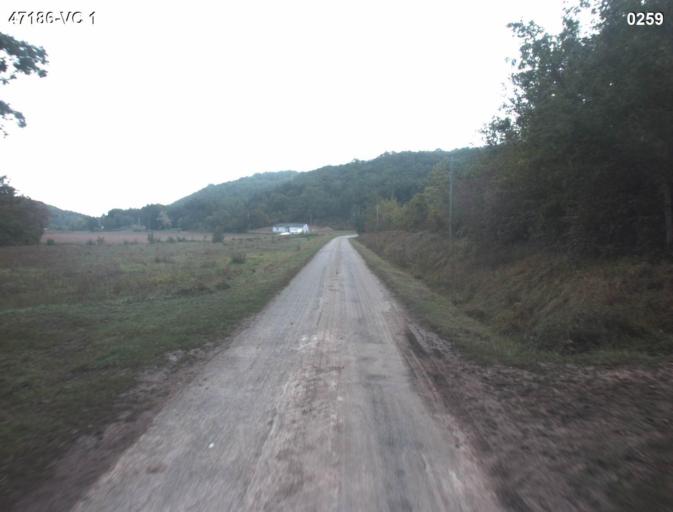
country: FR
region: Aquitaine
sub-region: Departement du Lot-et-Garonne
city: Sainte-Colombe-en-Bruilhois
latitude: 44.1908
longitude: 0.4431
